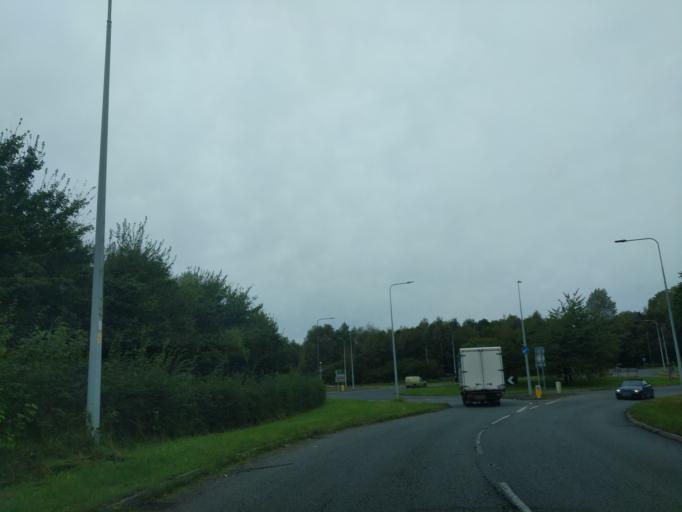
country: GB
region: England
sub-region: Cheshire East
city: Weston
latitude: 53.0575
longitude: -2.3991
